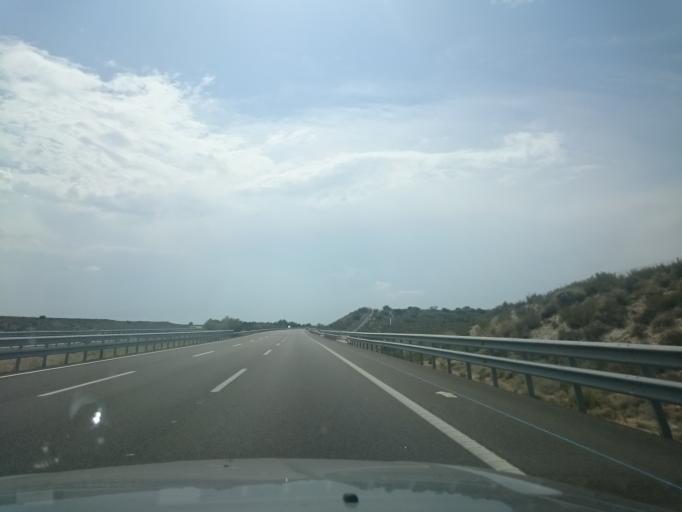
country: ES
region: Aragon
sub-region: Provincia de Huesca
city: Penalba
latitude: 41.5140
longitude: -0.0607
